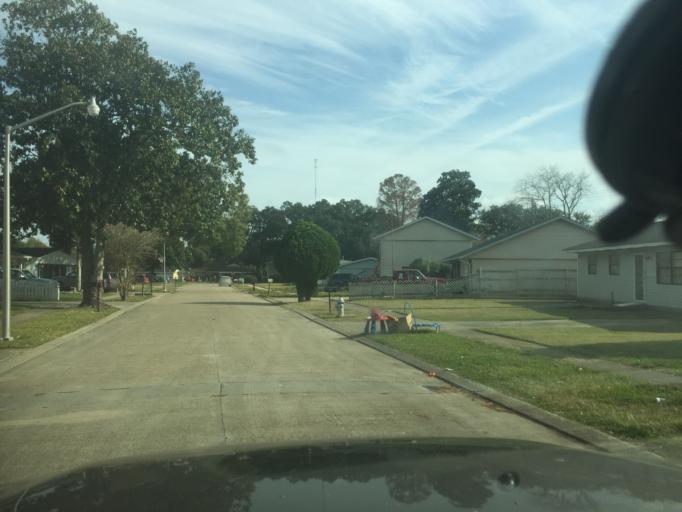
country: US
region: Louisiana
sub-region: Jefferson Parish
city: Avondale
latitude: 29.9125
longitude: -90.2033
